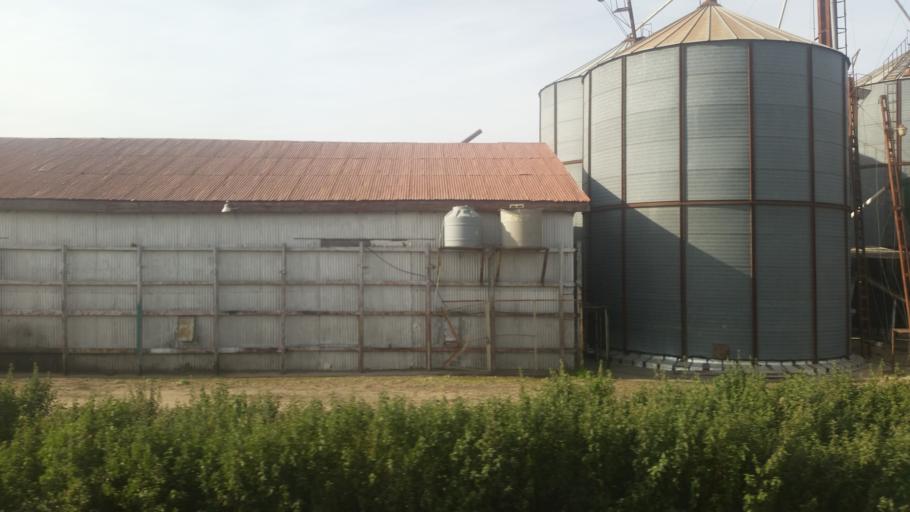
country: AR
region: Cordoba
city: Laguna Larga
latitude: -31.7790
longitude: -63.8010
